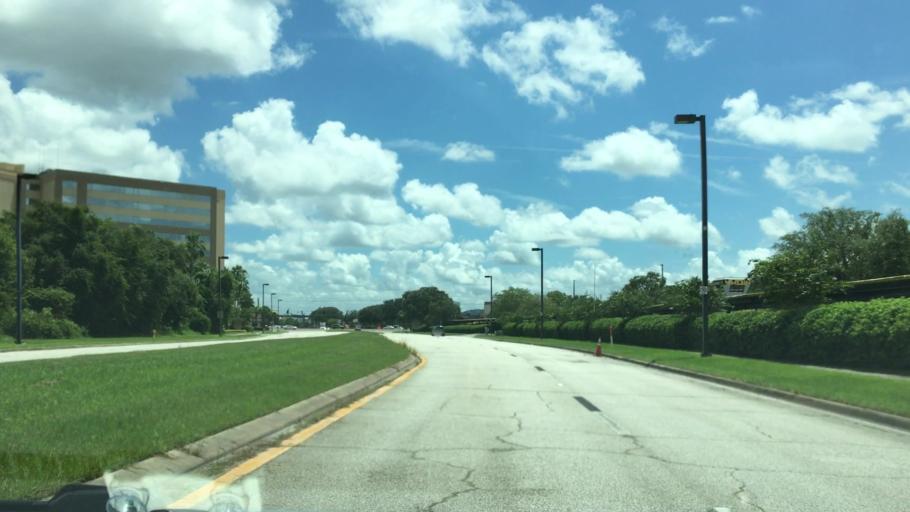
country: US
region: Florida
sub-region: Orange County
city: Conway
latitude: 28.4633
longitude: -81.3133
